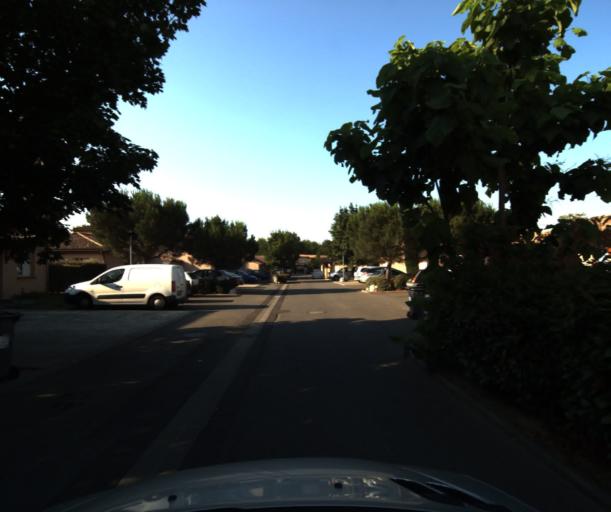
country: FR
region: Midi-Pyrenees
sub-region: Departement de la Haute-Garonne
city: Roquettes
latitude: 43.4816
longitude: 1.3867
